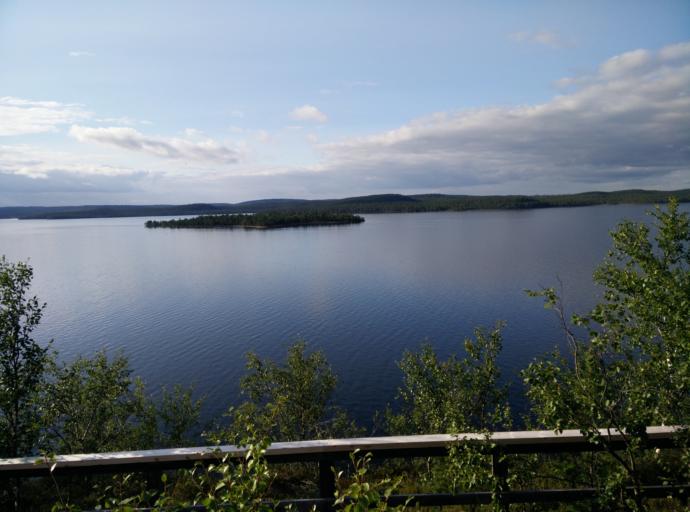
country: FI
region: Lapland
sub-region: Pohjois-Lappi
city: Inari
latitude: 68.9387
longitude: 27.2922
